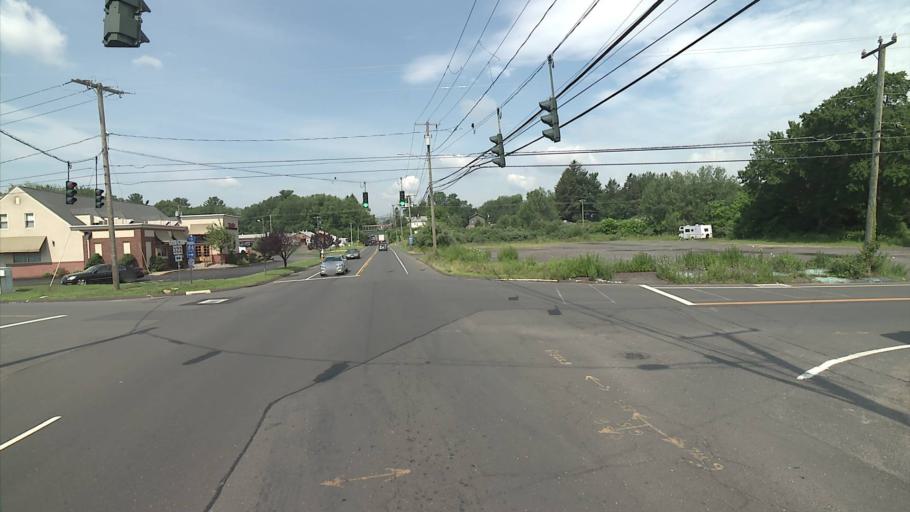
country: US
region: Connecticut
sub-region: New Haven County
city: Cheshire Village
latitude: 41.5643
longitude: -72.9006
